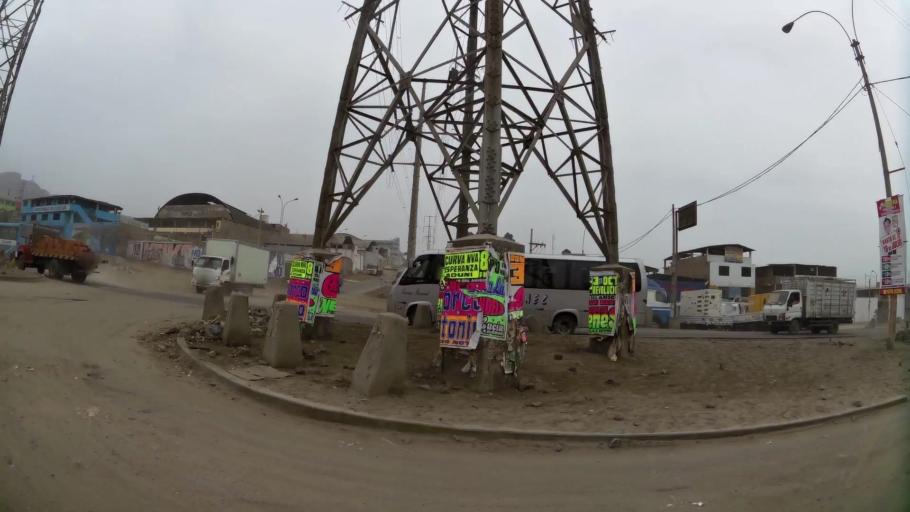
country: PE
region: Lima
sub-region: Lima
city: Surco
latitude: -12.1842
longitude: -76.9453
